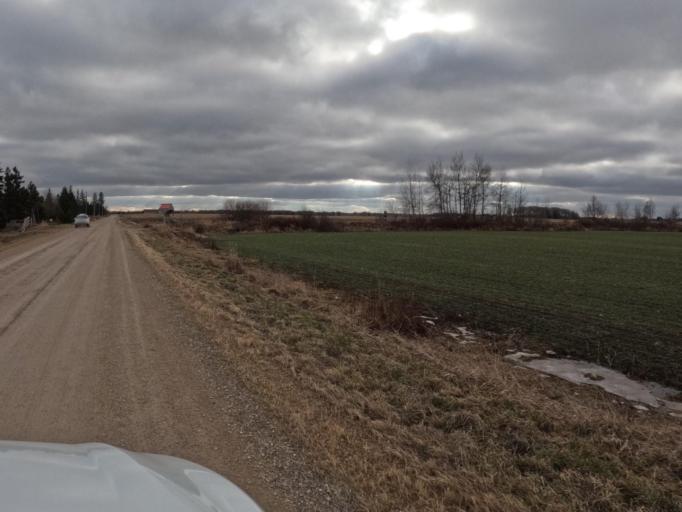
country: CA
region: Ontario
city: Shelburne
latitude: 43.8690
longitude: -80.4016
